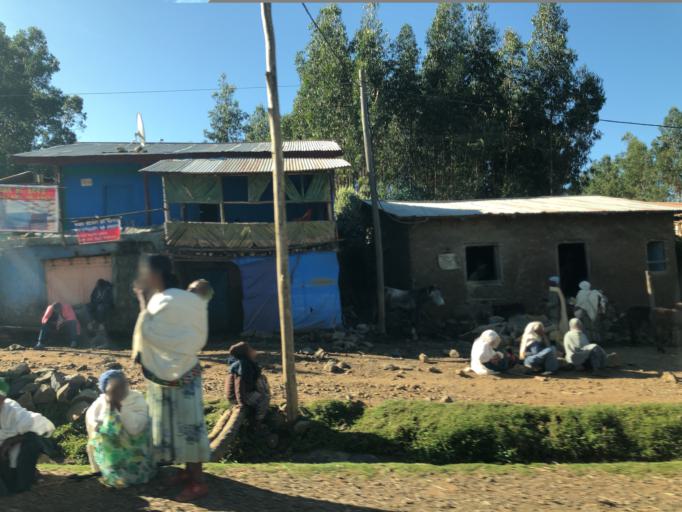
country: ET
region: Amhara
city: Debre Tabor
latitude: 11.8458
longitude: 38.0519
